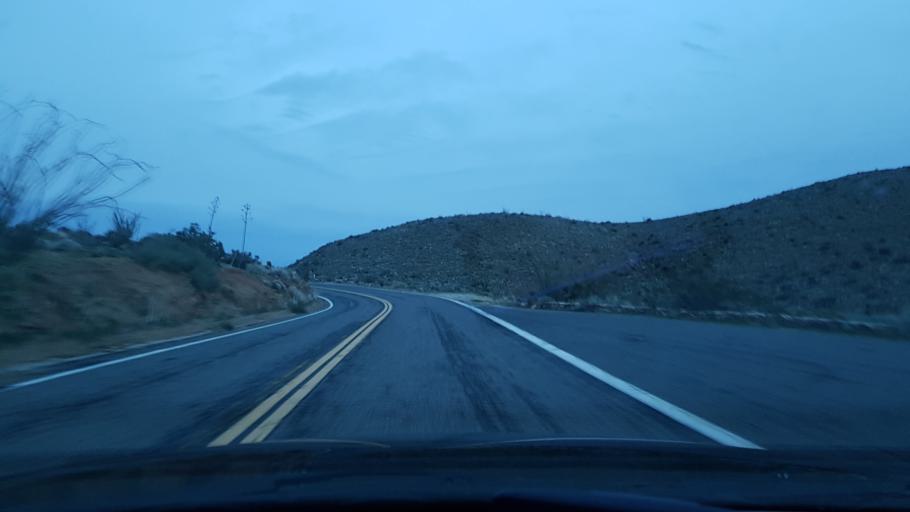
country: US
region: California
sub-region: San Diego County
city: Julian
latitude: 33.0153
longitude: -116.4433
